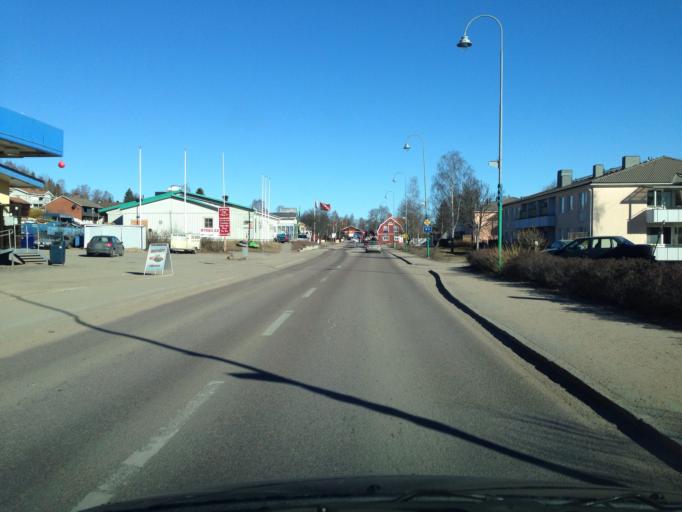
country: SE
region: Gaevleborg
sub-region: Ljusdals Kommun
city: Jaervsoe
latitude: 61.7160
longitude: 16.1697
